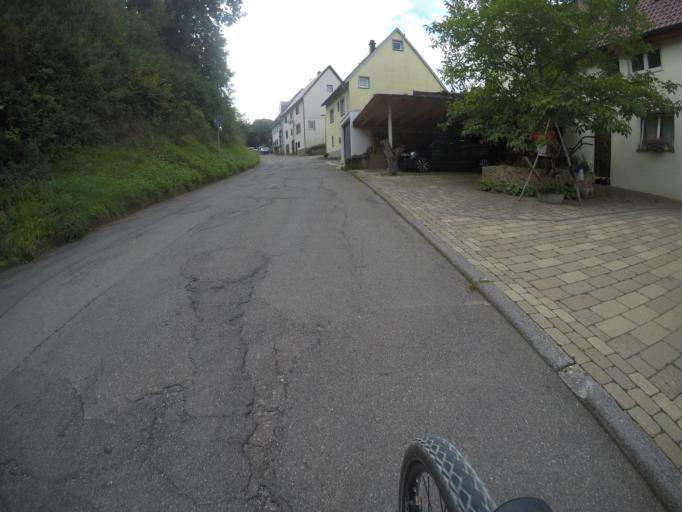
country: DE
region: Baden-Wuerttemberg
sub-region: Tuebingen Region
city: Munsingen
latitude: 48.4313
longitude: 9.4961
